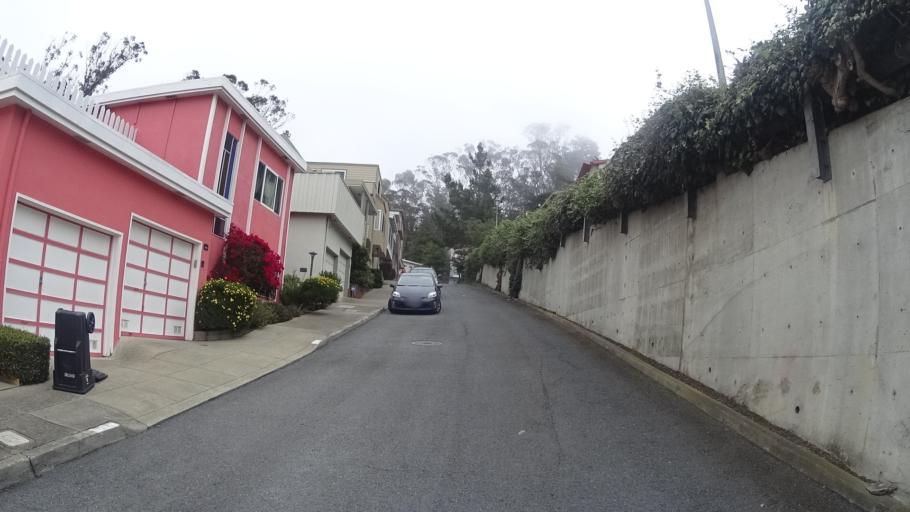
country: US
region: California
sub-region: San Mateo County
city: Daly City
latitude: 37.7377
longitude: -122.4589
